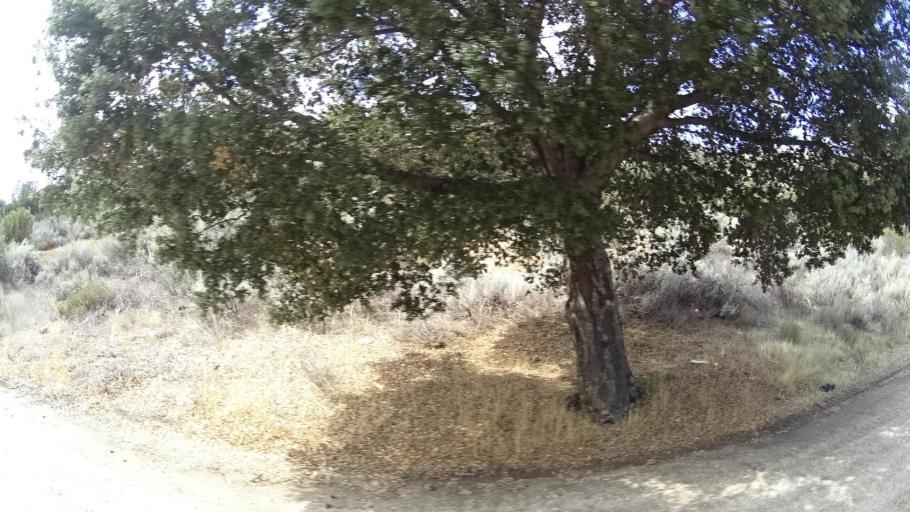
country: US
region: California
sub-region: San Diego County
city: Pine Valley
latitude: 32.7239
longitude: -116.4962
